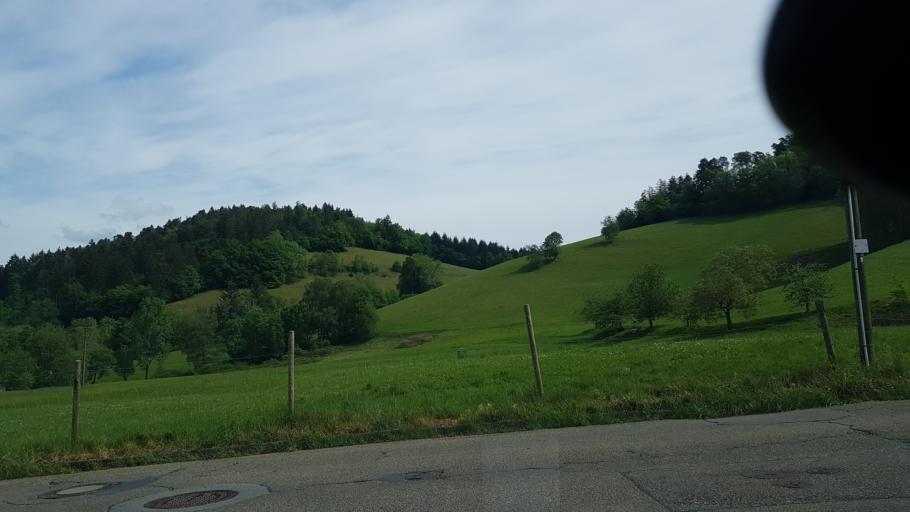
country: DE
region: Baden-Wuerttemberg
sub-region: Freiburg Region
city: Kirchzarten
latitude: 47.9527
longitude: 7.9133
